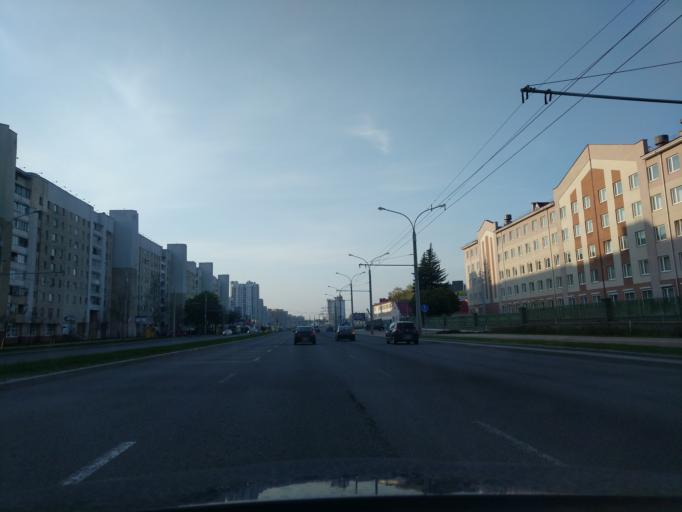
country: BY
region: Minsk
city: Minsk
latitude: 53.8671
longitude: 27.5706
